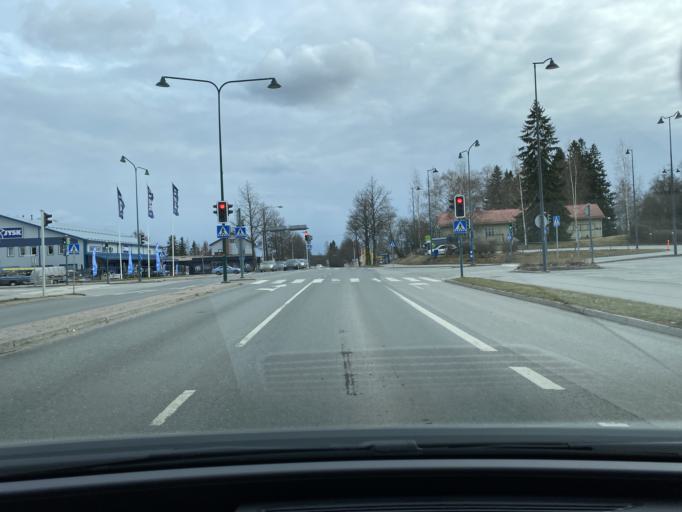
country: FI
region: Pirkanmaa
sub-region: Lounais-Pirkanmaa
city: Vammala
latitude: 61.3368
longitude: 22.9192
